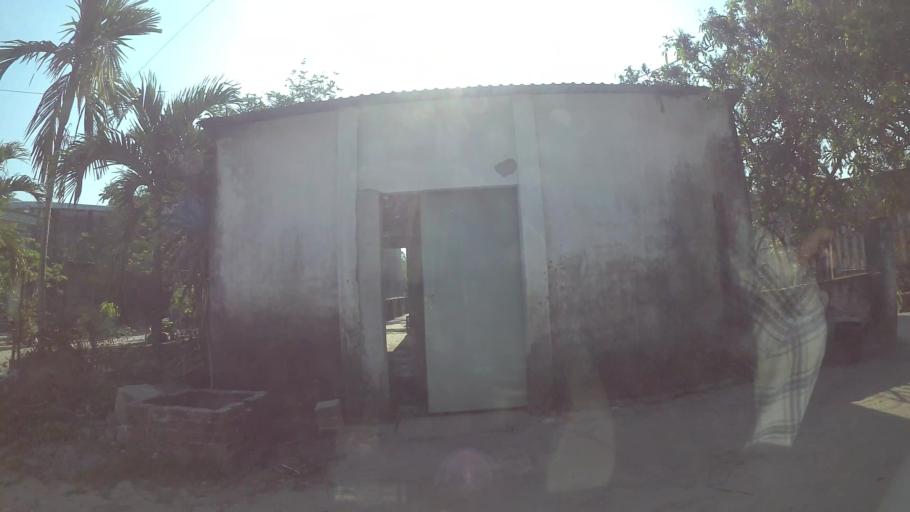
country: VN
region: Quang Nam
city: Quang Nam
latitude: 15.9506
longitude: 108.2670
